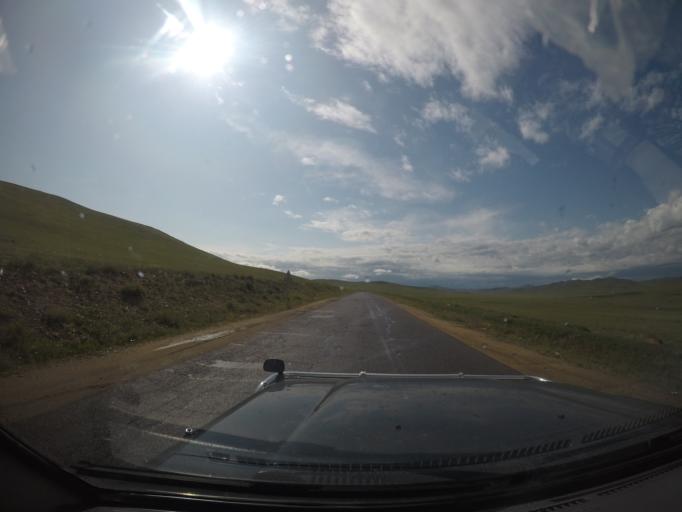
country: MN
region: Hentiy
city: Modot
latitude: 47.8095
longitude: 108.7977
